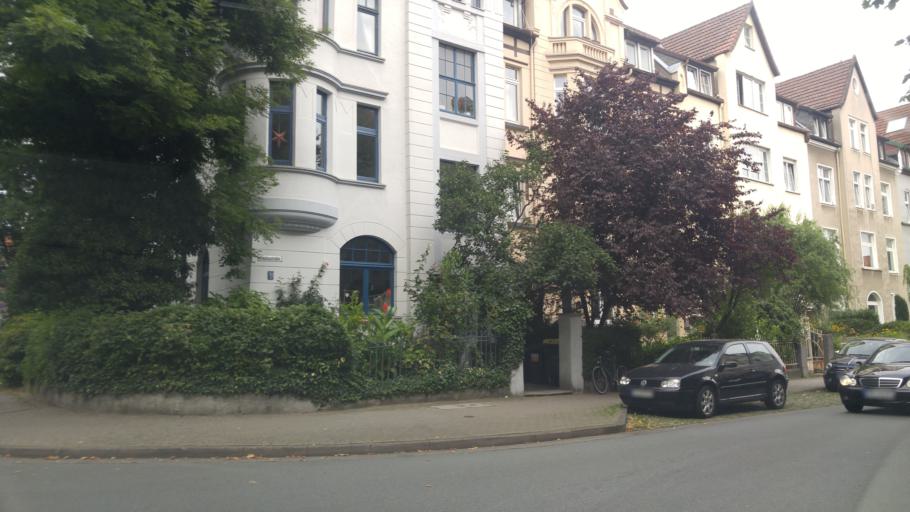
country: DE
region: North Rhine-Westphalia
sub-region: Regierungsbezirk Detmold
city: Bielefeld
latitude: 52.0271
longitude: 8.5409
